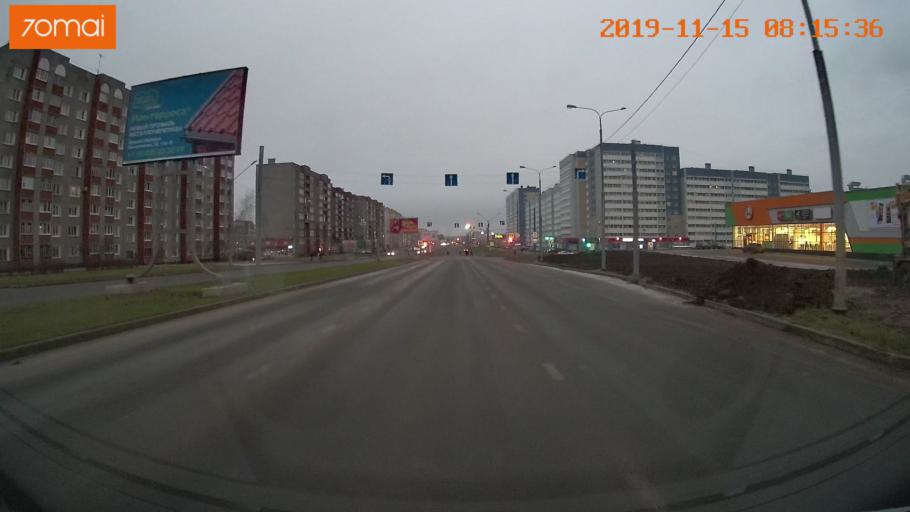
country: RU
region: Vologda
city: Cherepovets
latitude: 59.0837
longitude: 37.9214
